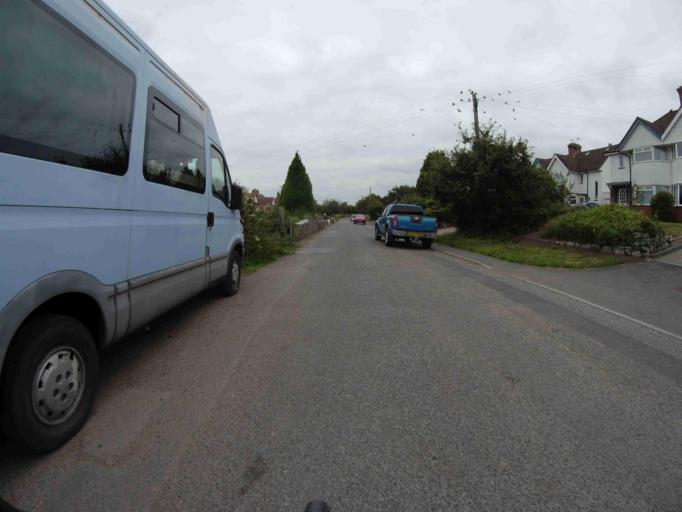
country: GB
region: England
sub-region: Devon
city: Topsham
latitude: 50.6904
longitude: -3.4683
